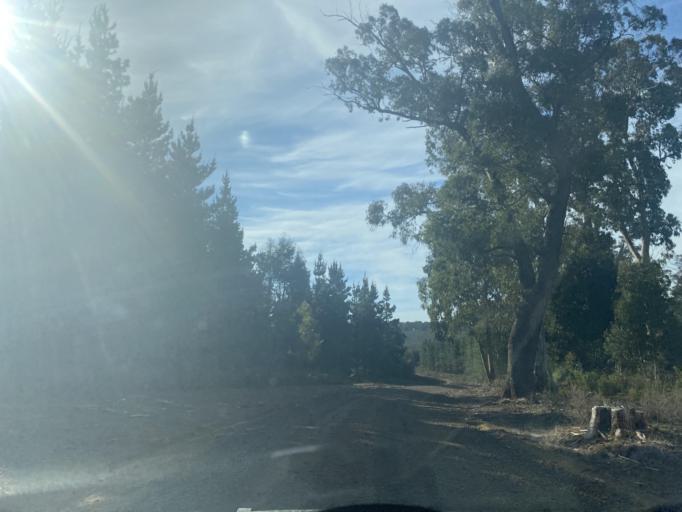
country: AU
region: Victoria
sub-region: Mansfield
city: Mansfield
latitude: -36.8705
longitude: 146.1779
